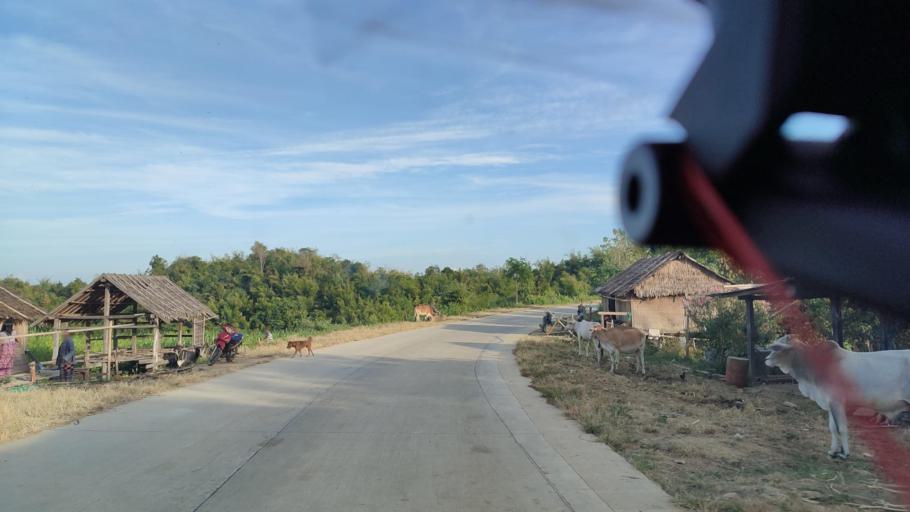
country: MM
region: Magway
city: Taungdwingyi
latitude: 20.0389
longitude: 95.7842
